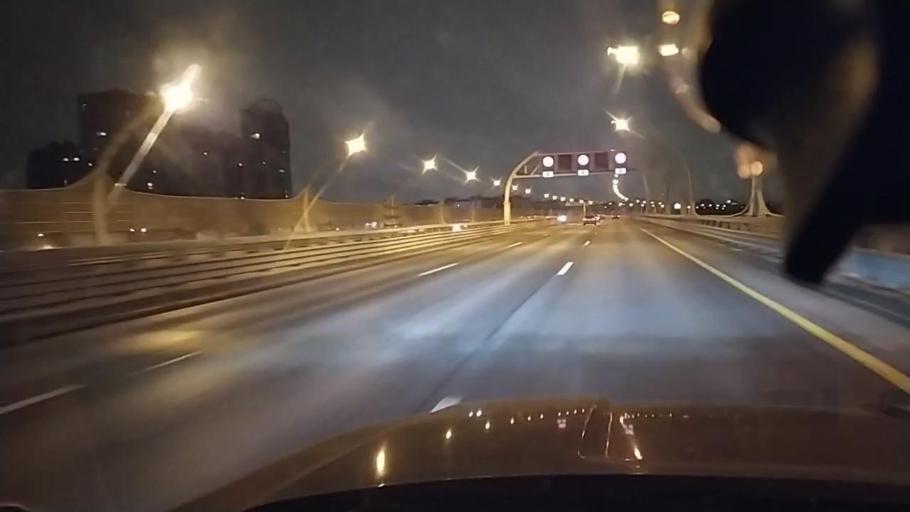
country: RU
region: Leningrad
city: Untolovo
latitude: 60.0237
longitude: 30.2135
